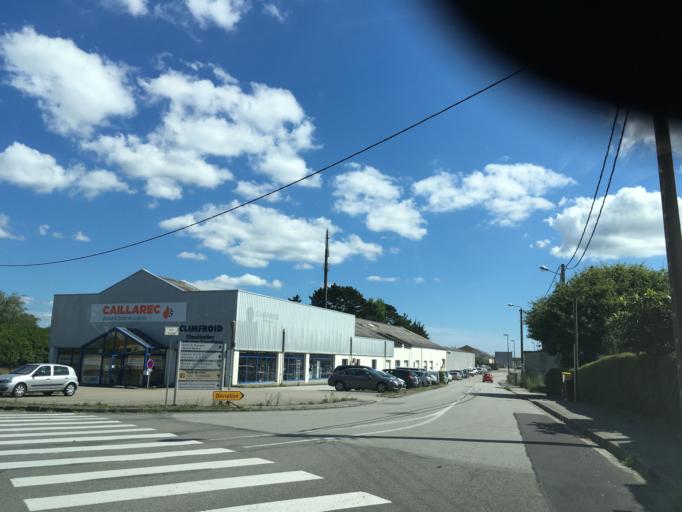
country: FR
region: Brittany
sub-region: Departement du Finistere
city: Ergue-Gaberic
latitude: 47.9847
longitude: -4.0598
